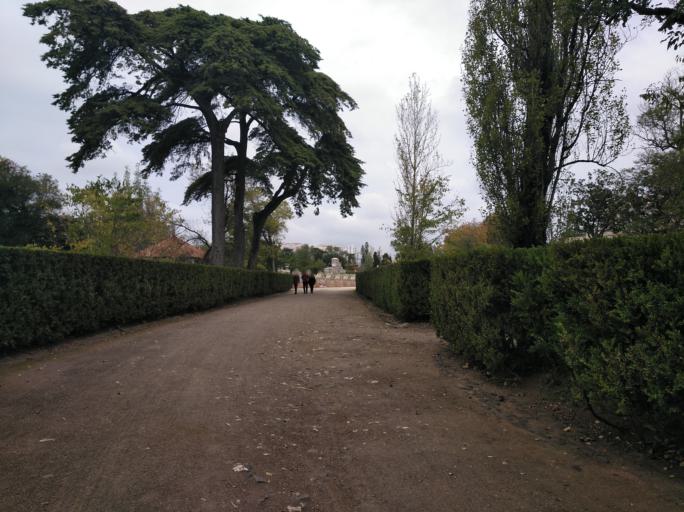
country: PT
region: Lisbon
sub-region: Sintra
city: Queluz
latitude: 38.7494
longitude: -9.2602
